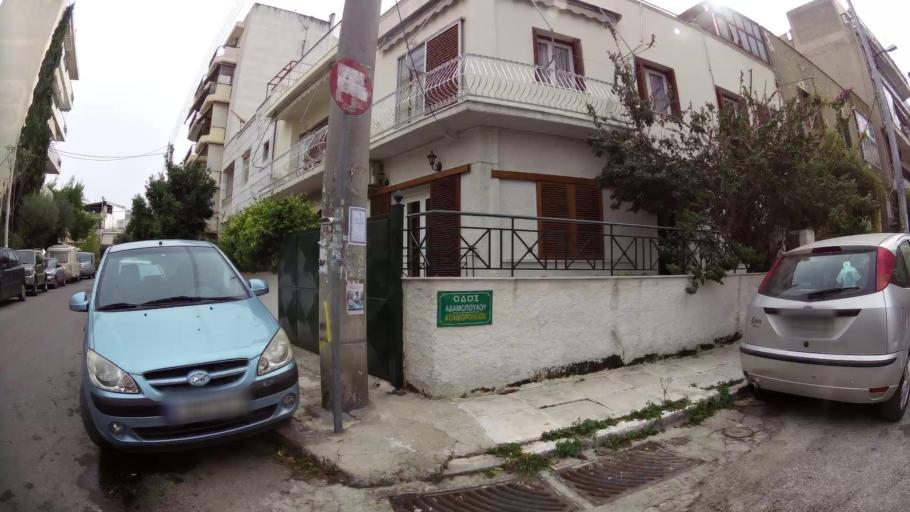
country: GR
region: Attica
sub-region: Nomarchia Athinas
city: Nea Ionia
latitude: 38.0321
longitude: 23.7568
